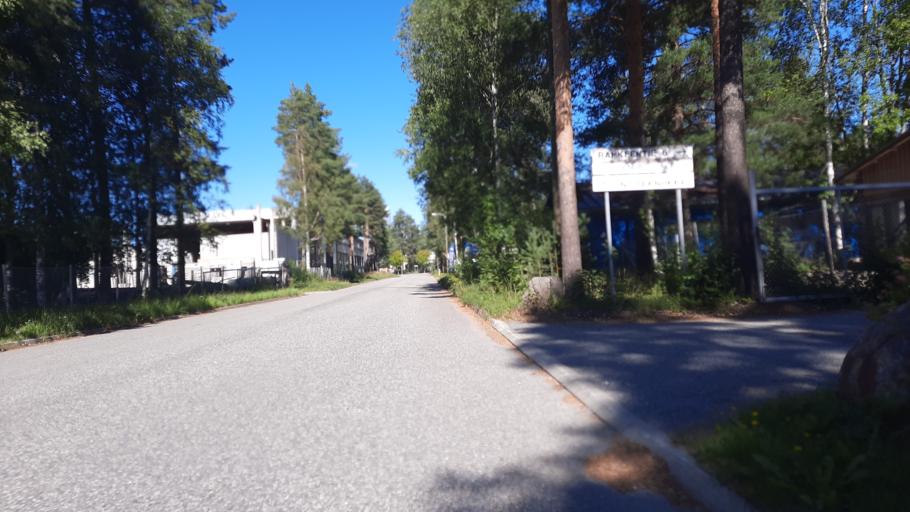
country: FI
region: North Karelia
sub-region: Joensuu
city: Joensuu
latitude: 62.6194
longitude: 29.7560
